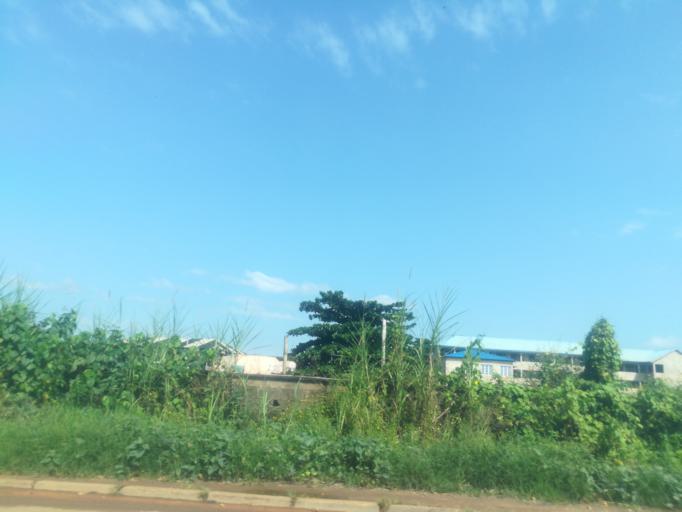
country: NG
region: Oyo
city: Ibadan
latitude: 7.4176
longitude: 3.9647
